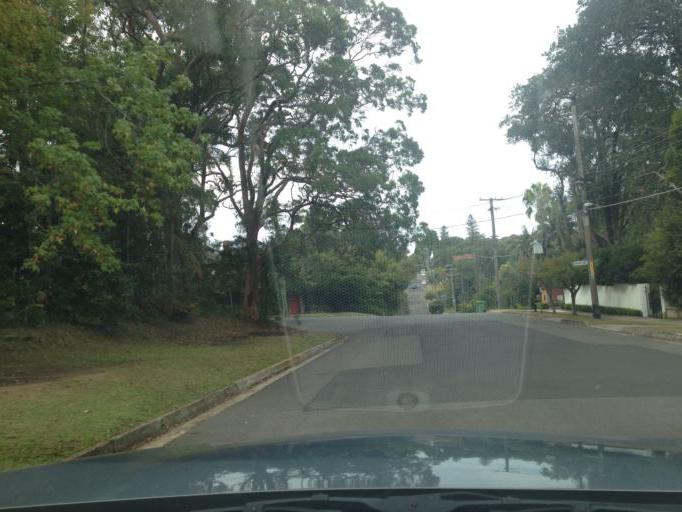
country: AU
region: New South Wales
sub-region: Ku-ring-gai
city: Killara
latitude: -33.7668
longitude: 151.1692
